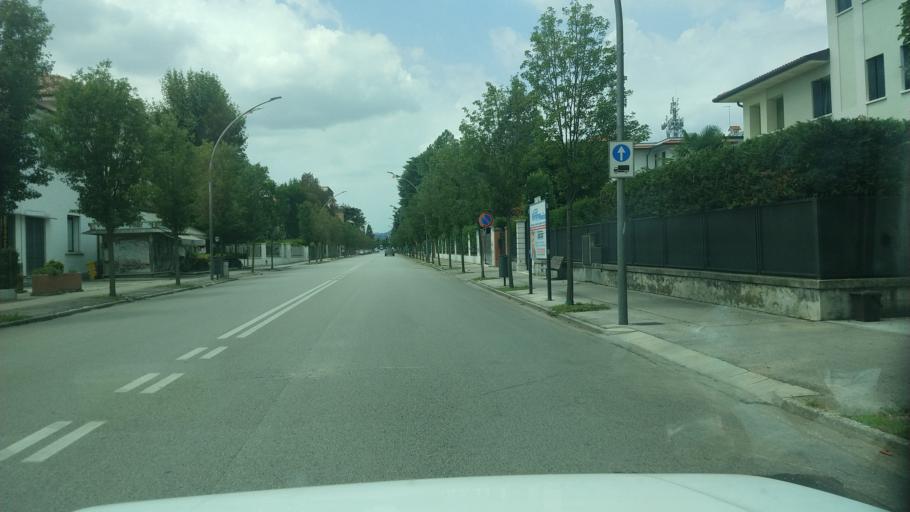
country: IT
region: Veneto
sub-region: Provincia di Vicenza
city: Bassano del Grappa
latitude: 45.7695
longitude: 11.7472
